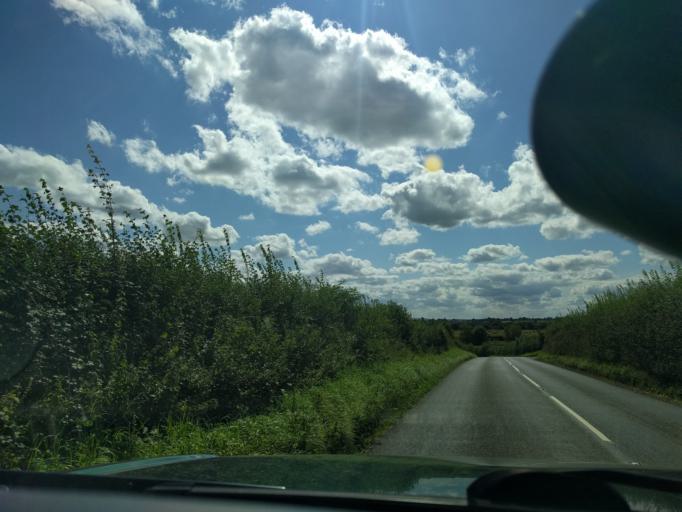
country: GB
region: England
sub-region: Wiltshire
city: Box
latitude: 51.3899
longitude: -2.2341
